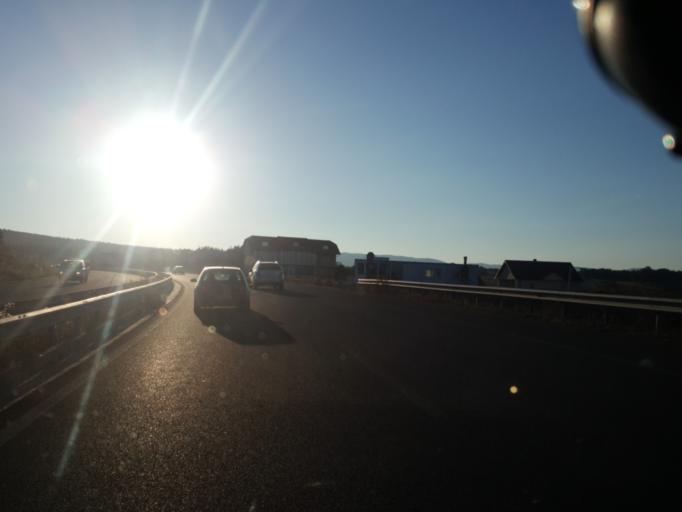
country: XK
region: Prizren
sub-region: Komuna e Malisheves
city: Llazice
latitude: 42.5650
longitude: 20.7645
